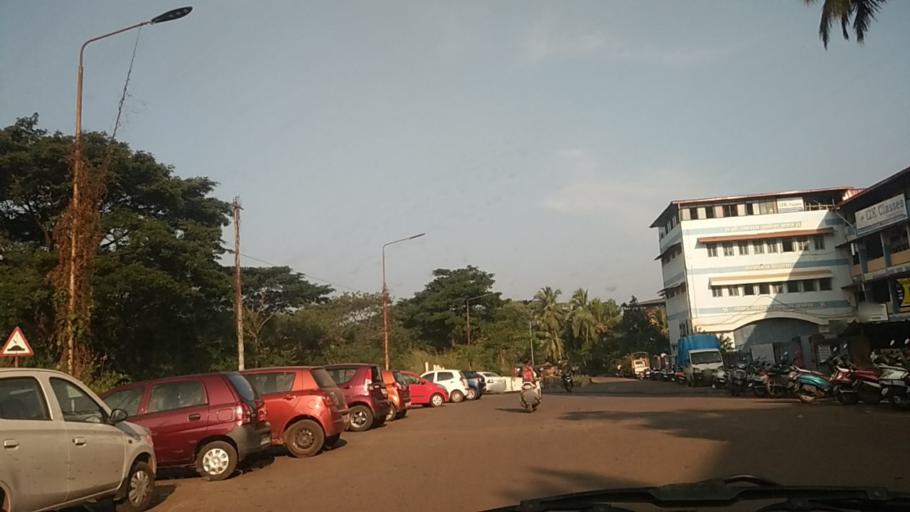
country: IN
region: Goa
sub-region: South Goa
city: Madgaon
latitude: 15.2739
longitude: 73.9536
